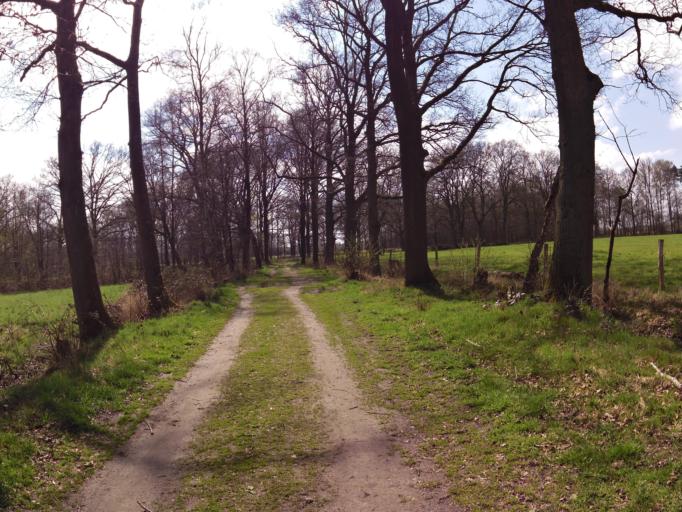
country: NL
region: North Brabant
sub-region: Gemeente Haaren
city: Haaren
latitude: 51.5547
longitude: 5.2655
